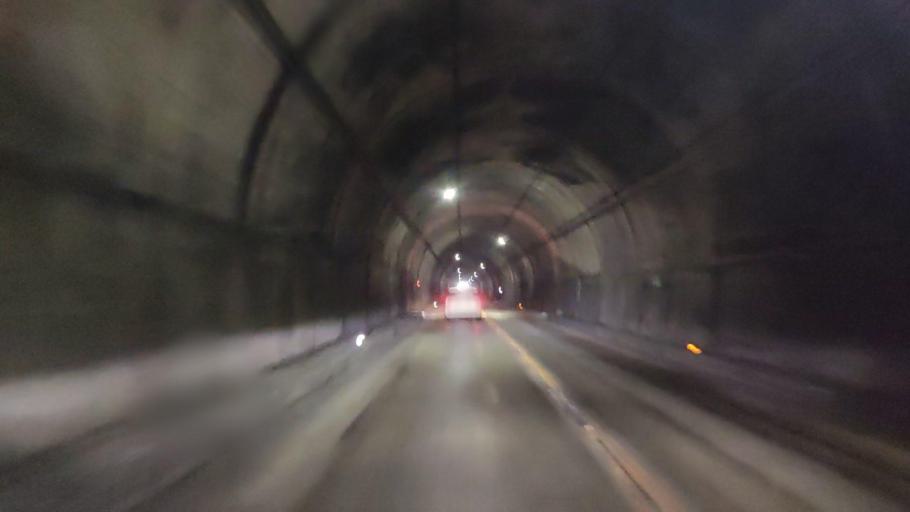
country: JP
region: Nara
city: Yoshino-cho
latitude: 34.3695
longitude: 135.9152
